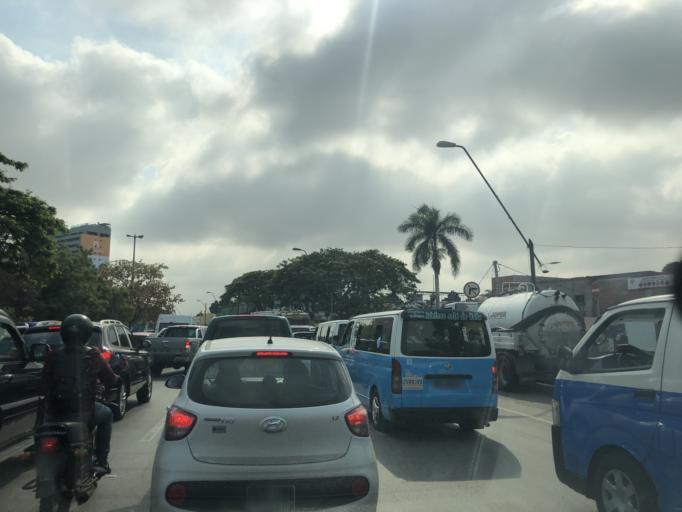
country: AO
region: Luanda
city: Luanda
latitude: -8.8390
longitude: 13.2347
